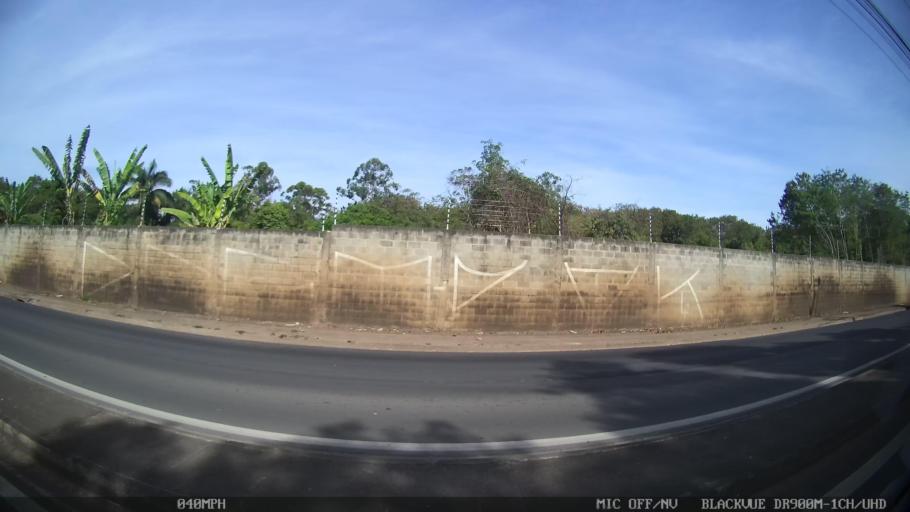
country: BR
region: Sao Paulo
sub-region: Piracicaba
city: Piracicaba
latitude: -22.7203
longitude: -47.6742
